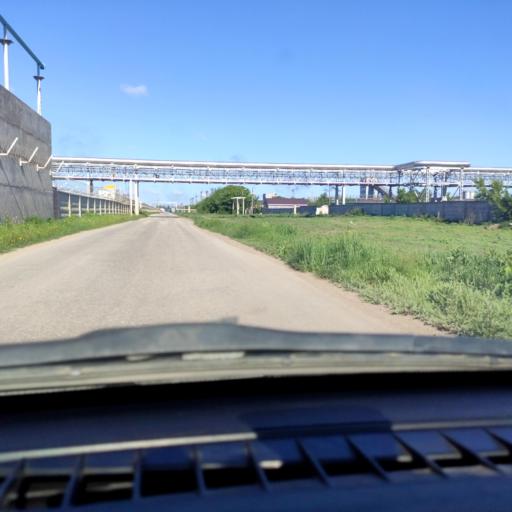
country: RU
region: Samara
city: Tol'yatti
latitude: 53.5554
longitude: 49.4767
